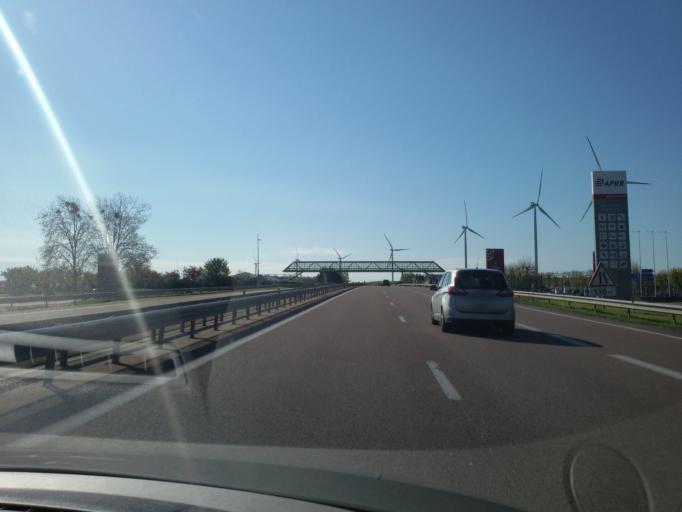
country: FR
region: Bourgogne
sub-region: Departement de l'Yonne
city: Venoy
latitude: 47.7910
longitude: 3.6691
